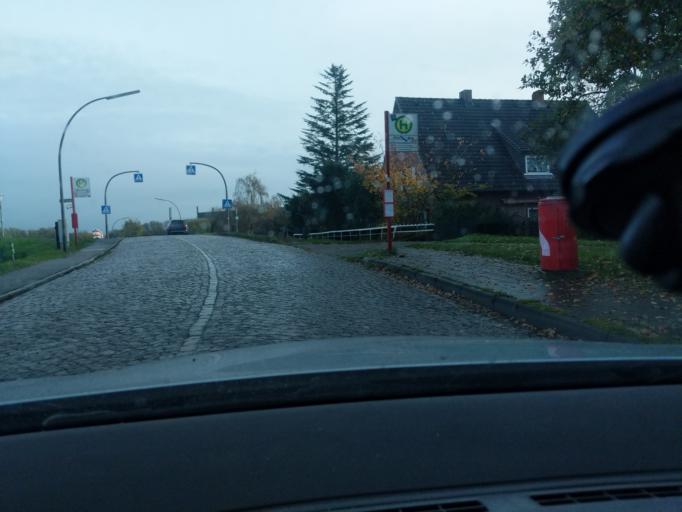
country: DE
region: Lower Saxony
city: Neu Wulmstorf
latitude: 53.5317
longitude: 9.7781
